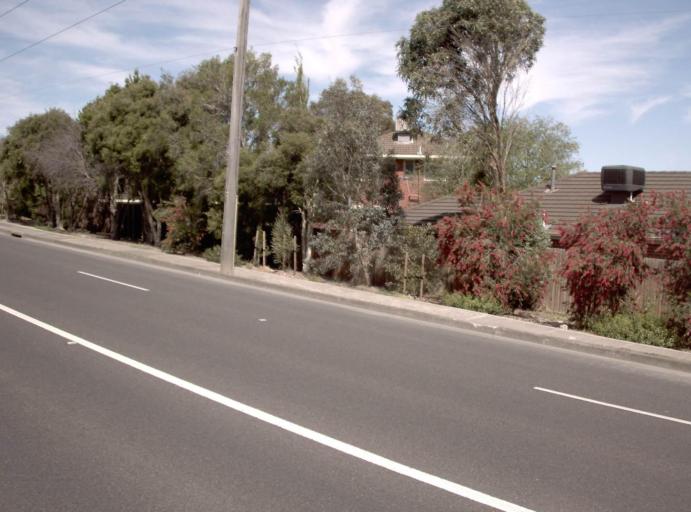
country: AU
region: Victoria
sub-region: Manningham
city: Donvale
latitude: -37.7704
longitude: 145.1651
